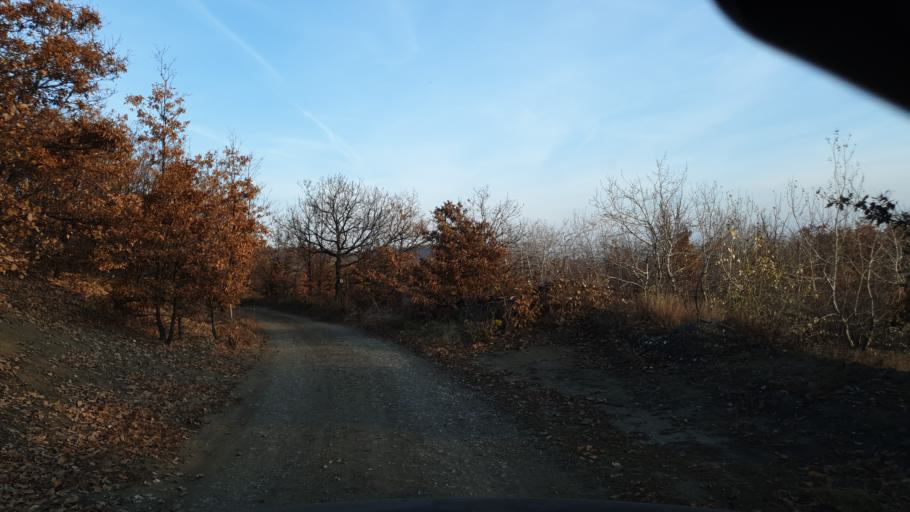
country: RS
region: Central Serbia
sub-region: Borski Okrug
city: Bor
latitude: 44.0730
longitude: 22.0665
